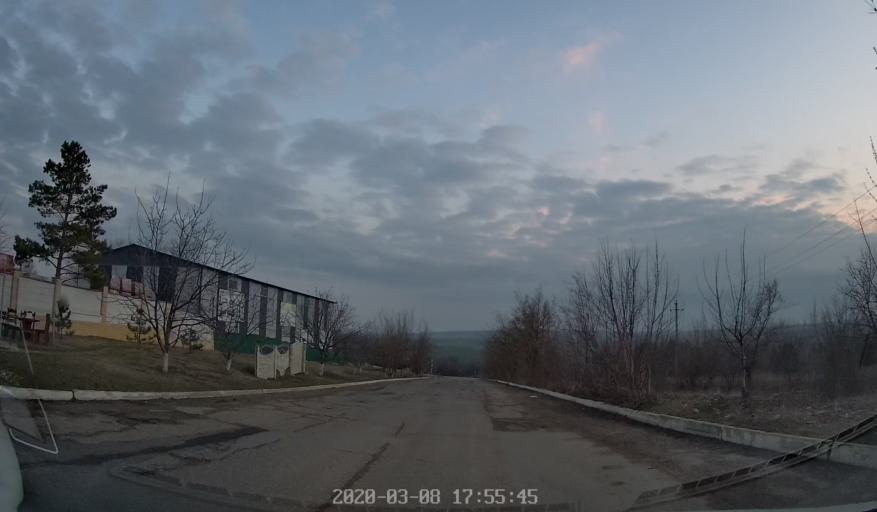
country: MD
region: Rezina
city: Rezina
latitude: 47.7504
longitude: 28.9490
